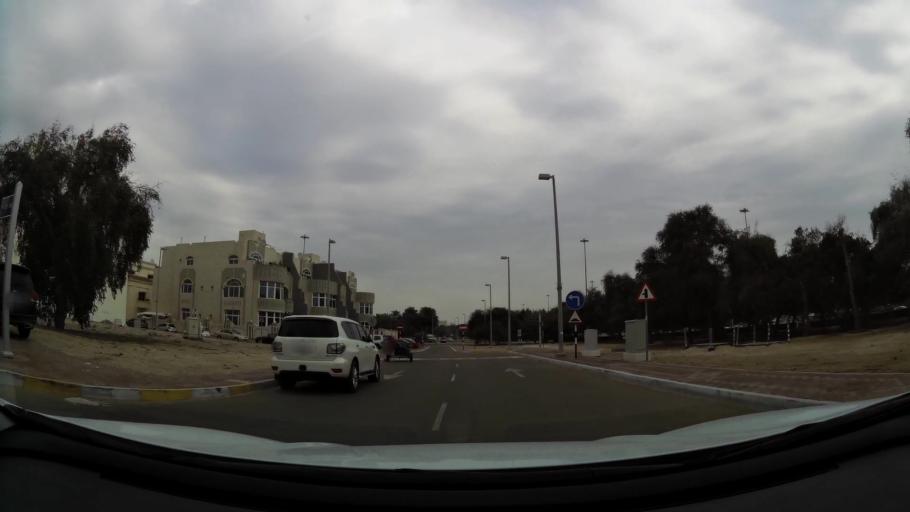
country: AE
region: Abu Dhabi
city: Abu Dhabi
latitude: 24.4375
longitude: 54.4039
